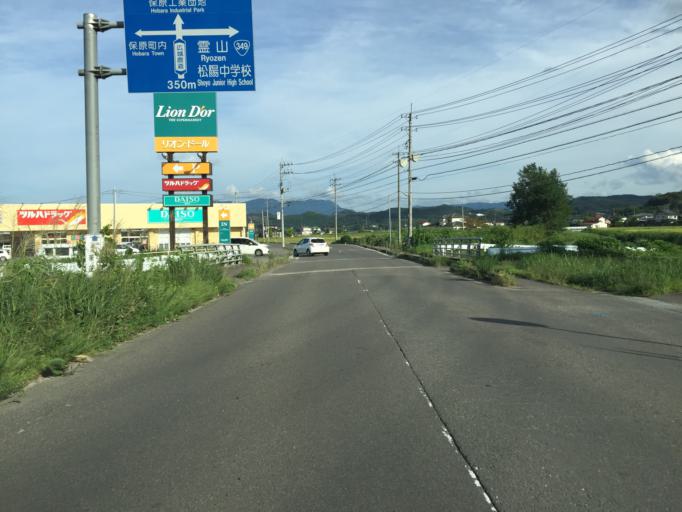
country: JP
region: Fukushima
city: Hobaramachi
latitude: 37.8092
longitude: 140.5470
